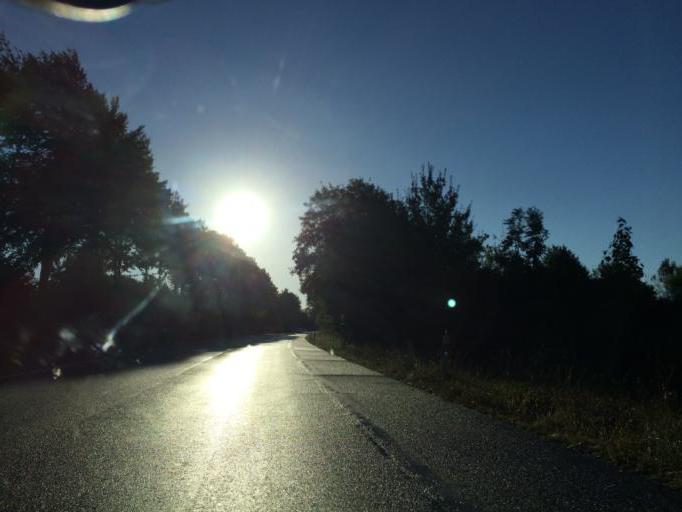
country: DE
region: North Rhine-Westphalia
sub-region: Regierungsbezirk Koln
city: Bad Honnef
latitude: 50.7030
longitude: 7.2669
